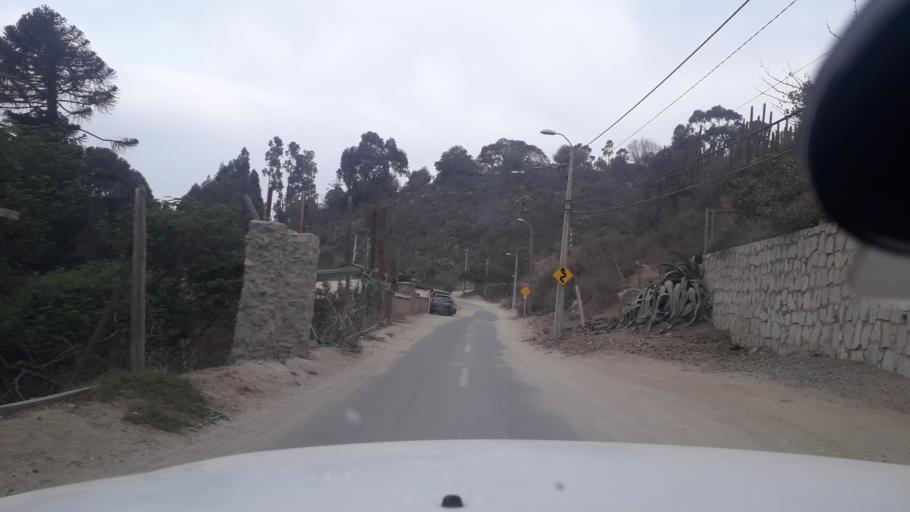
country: CL
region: Valparaiso
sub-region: Provincia de Valparaiso
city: Valparaiso
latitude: -33.1060
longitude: -71.6665
